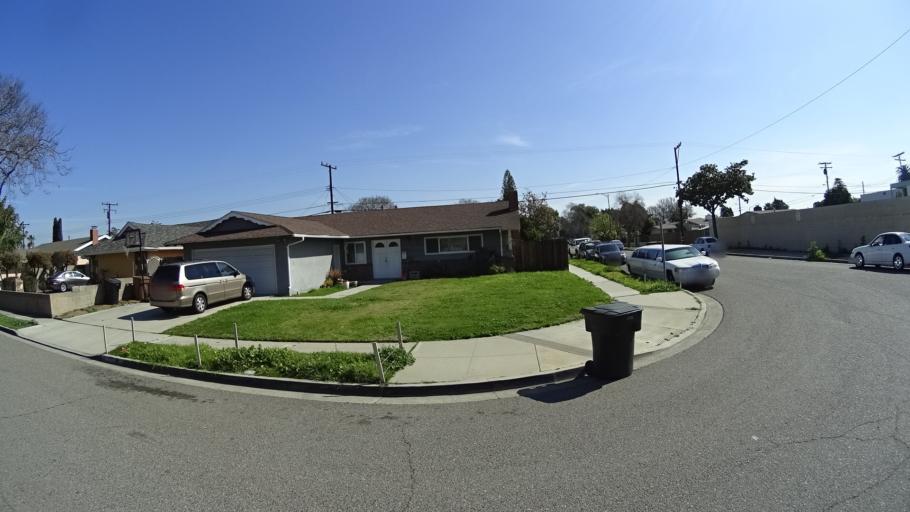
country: US
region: California
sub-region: Orange County
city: Fullerton
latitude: 33.8479
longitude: -117.9573
